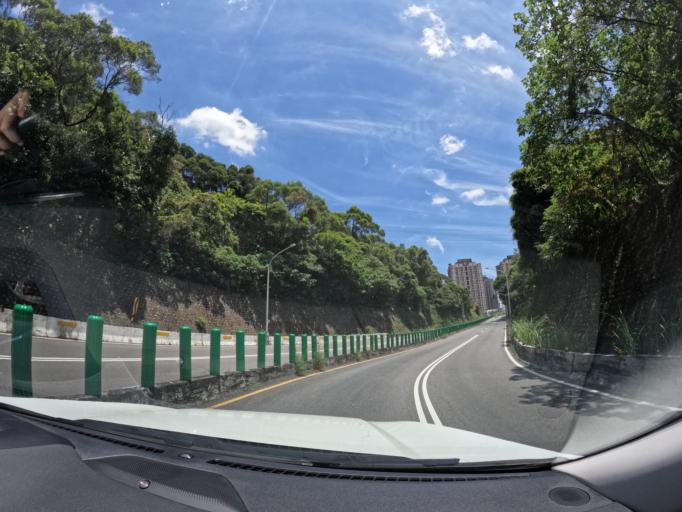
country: TW
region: Taiwan
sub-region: Taoyuan
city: Taoyuan
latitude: 25.0368
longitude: 121.3864
